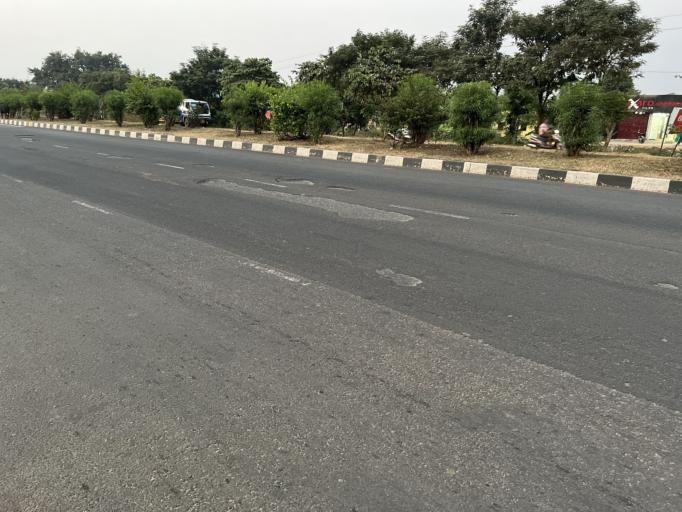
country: IN
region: Odisha
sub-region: Cuttack
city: Cuttack
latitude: 20.3925
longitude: 85.8837
